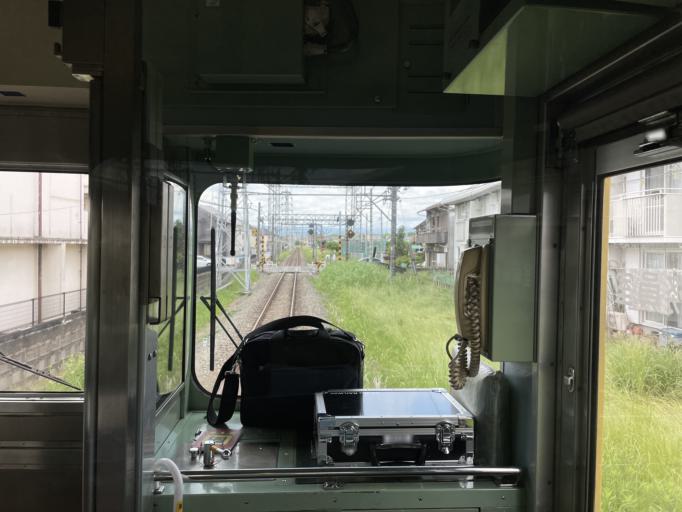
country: JP
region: Tokyo
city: Fussa
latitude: 35.7256
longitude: 139.3641
